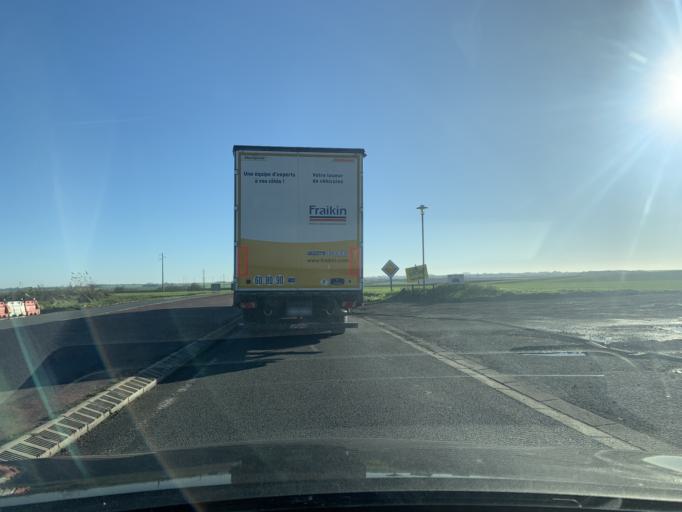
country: FR
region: Nord-Pas-de-Calais
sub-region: Departement du Nord
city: Escaudoeuvres
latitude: 50.1624
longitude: 3.2879
